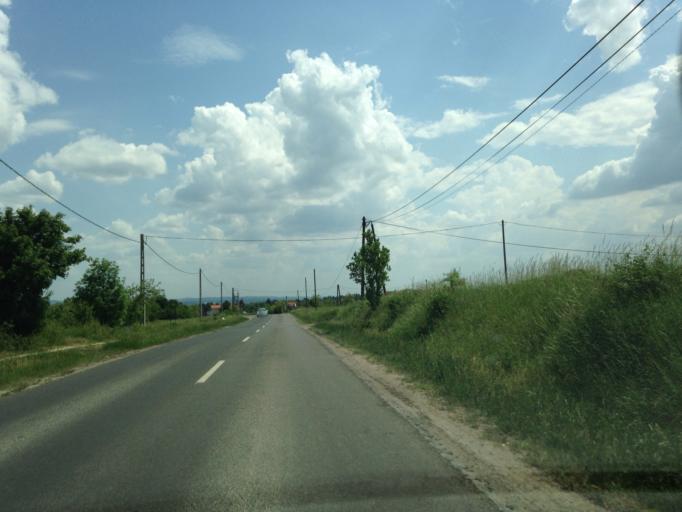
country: HU
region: Pest
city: Szentendre
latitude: 47.6868
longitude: 19.0565
